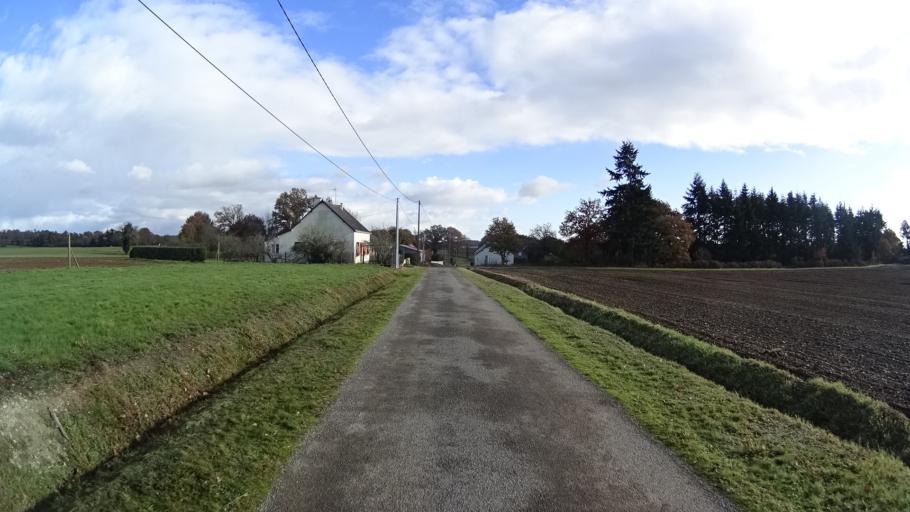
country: FR
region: Brittany
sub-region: Departement du Morbihan
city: La Gacilly
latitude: 47.7838
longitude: -2.1341
